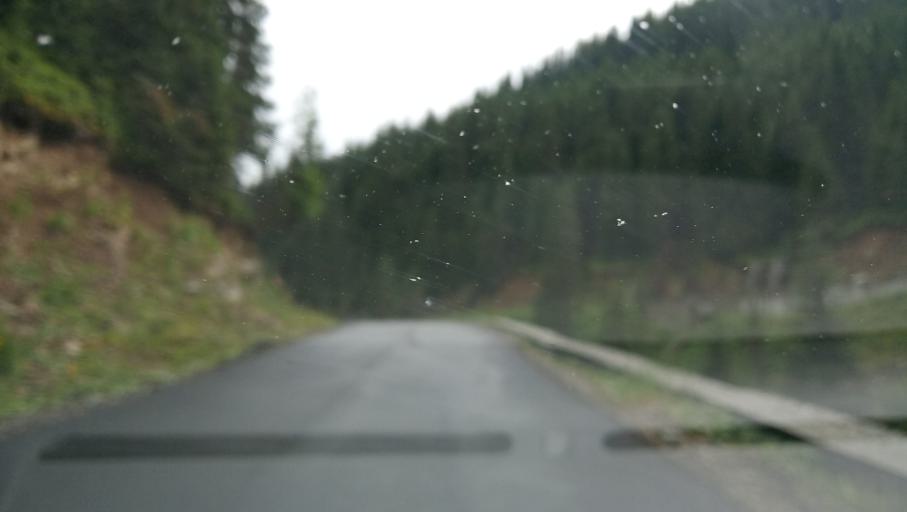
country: RO
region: Hunedoara
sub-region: Oras Petrila
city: Petrila
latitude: 45.4105
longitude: 23.5961
